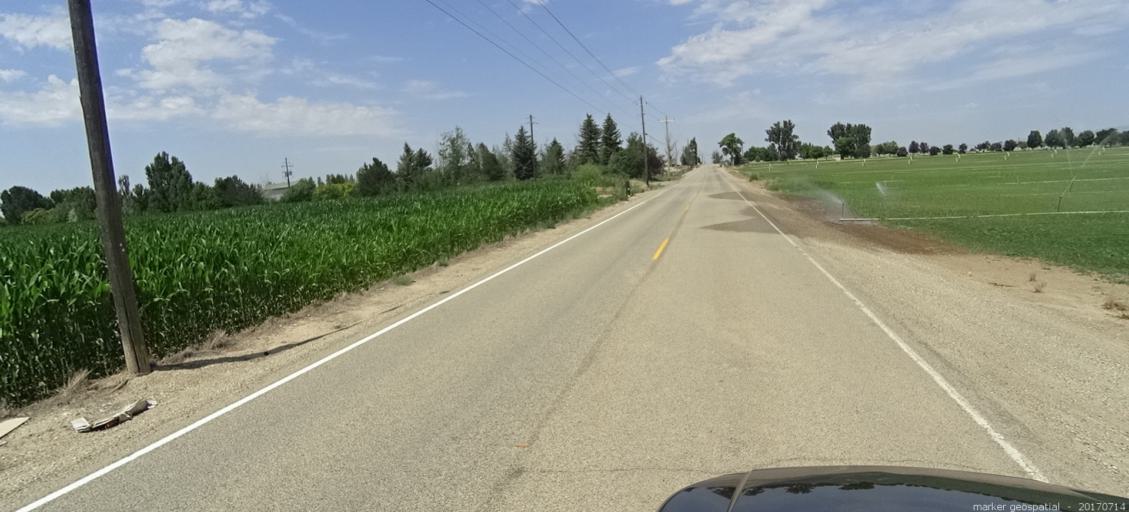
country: US
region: Idaho
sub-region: Ada County
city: Kuna
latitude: 43.5366
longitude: -116.3543
